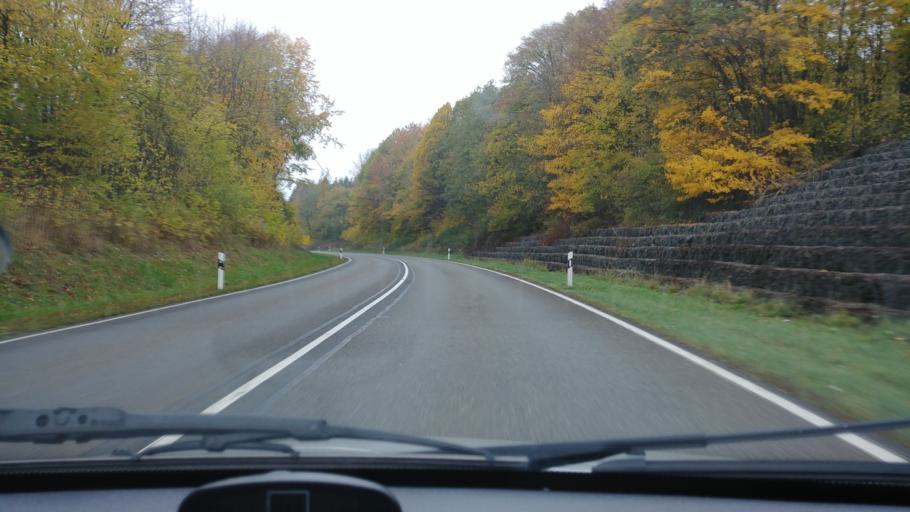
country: DE
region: Rheinland-Pfalz
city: Langenhahn
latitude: 50.5841
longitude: 7.9261
